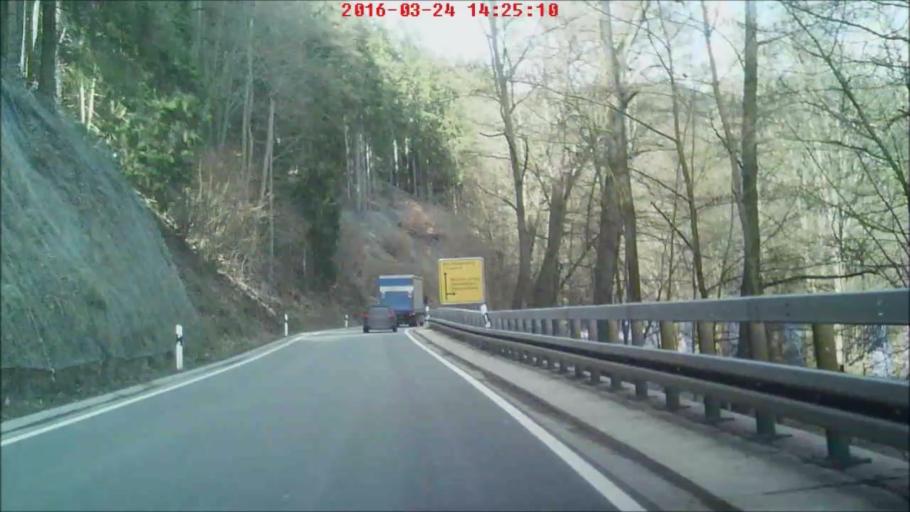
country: DE
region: Thuringia
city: Unterweissbach
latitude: 50.6240
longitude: 11.1524
